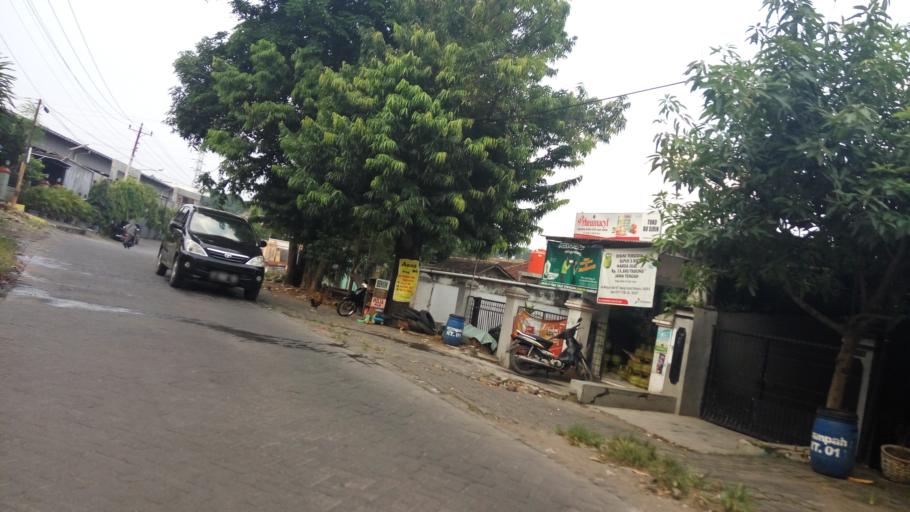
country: ID
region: Central Java
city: Semarang
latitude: -7.0158
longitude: 110.3840
